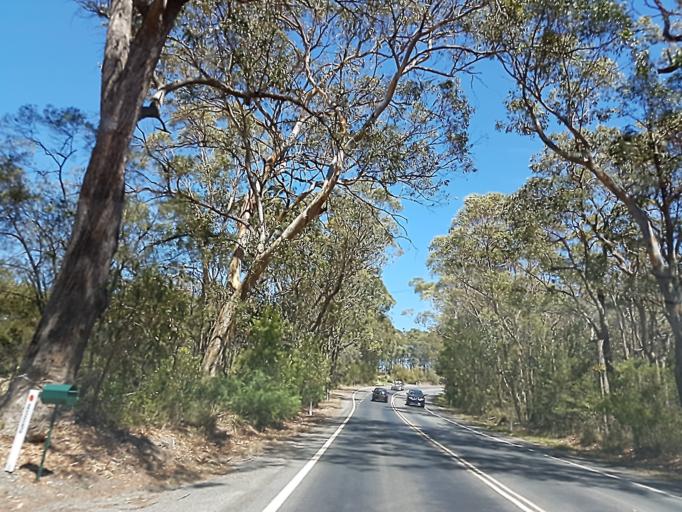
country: AU
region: New South Wales
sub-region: Hornsby Shire
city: Glenorie
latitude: -33.4697
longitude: 151.0052
